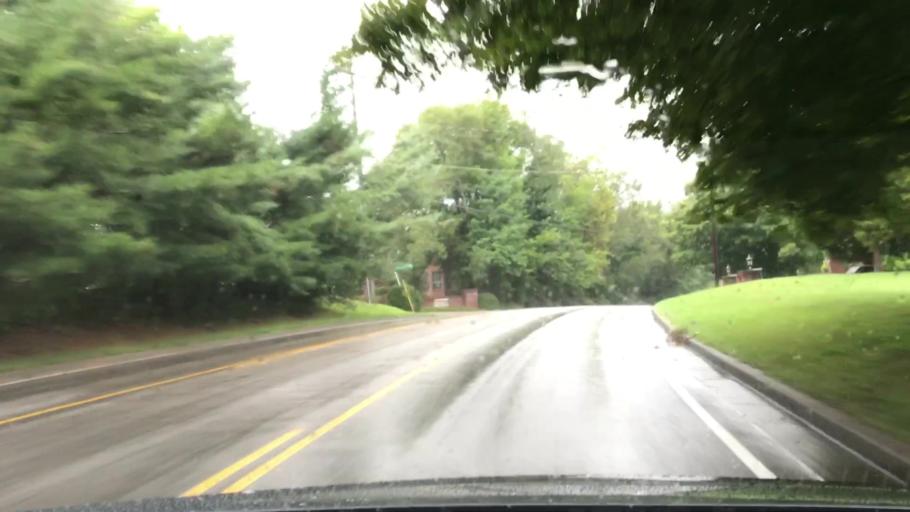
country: US
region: Tennessee
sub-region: Williamson County
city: Brentwood Estates
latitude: 36.0315
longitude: -86.7552
